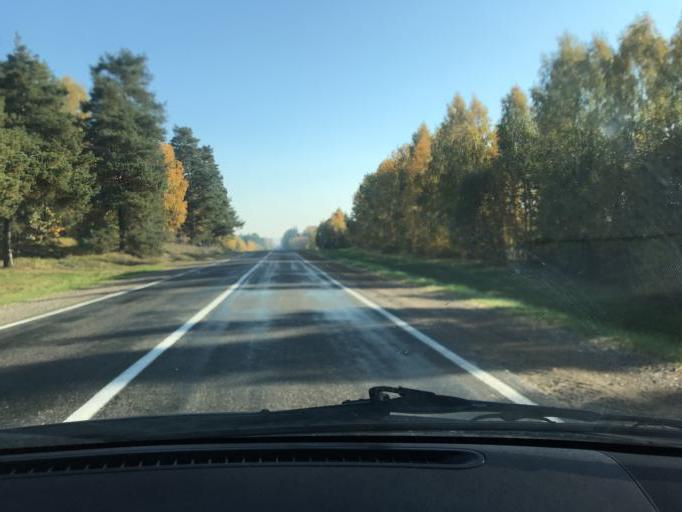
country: BY
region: Brest
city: Lyakhavichy
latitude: 52.9613
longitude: 26.4248
